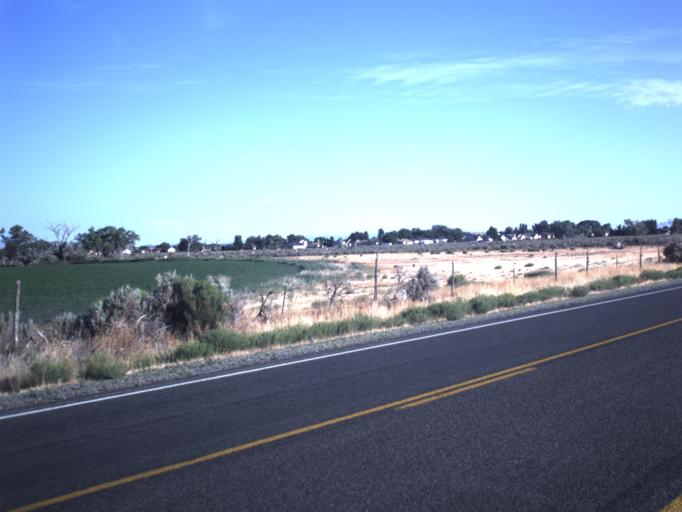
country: US
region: Utah
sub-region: Iron County
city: Enoch
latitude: 37.7559
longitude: -113.0552
